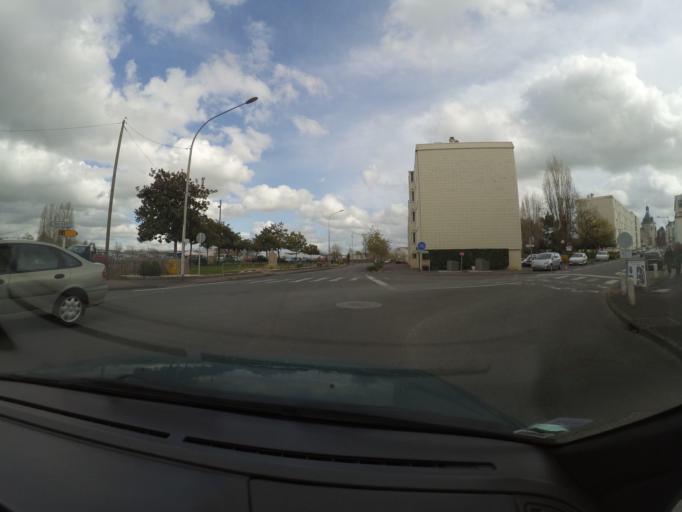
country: FR
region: Pays de la Loire
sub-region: Departement de la Loire-Atlantique
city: Ancenis
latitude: 47.3683
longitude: -1.1767
